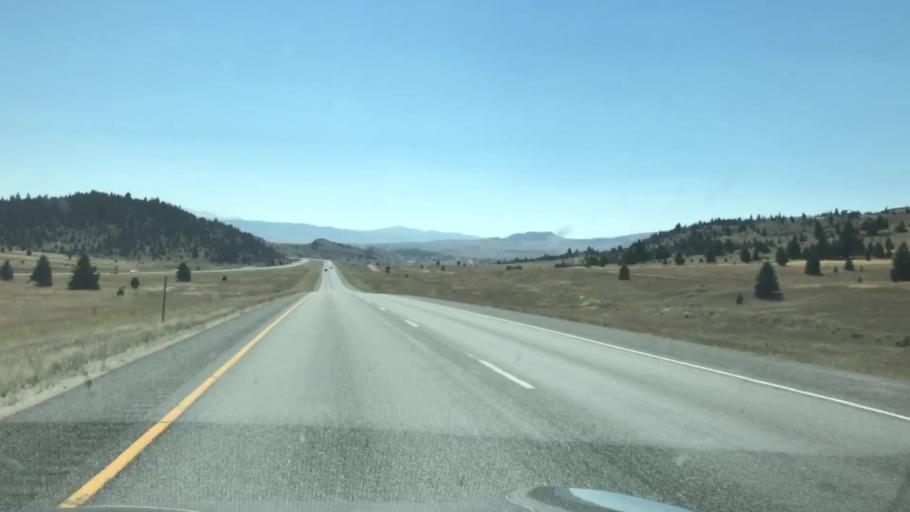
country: US
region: Montana
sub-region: Silver Bow County
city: Butte-Silver Bow (Balance)
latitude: 46.0351
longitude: -112.7350
